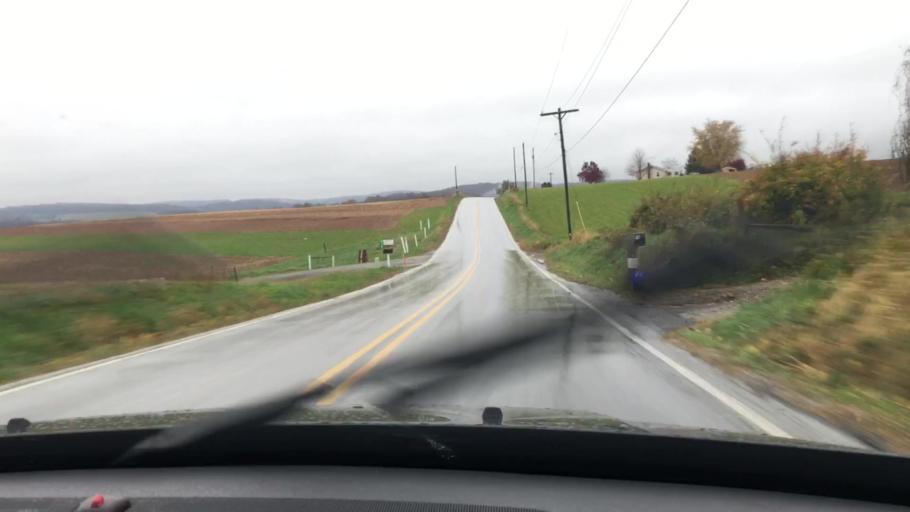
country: US
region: Pennsylvania
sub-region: York County
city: Susquehanna Trails
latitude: 39.8043
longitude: -76.4129
